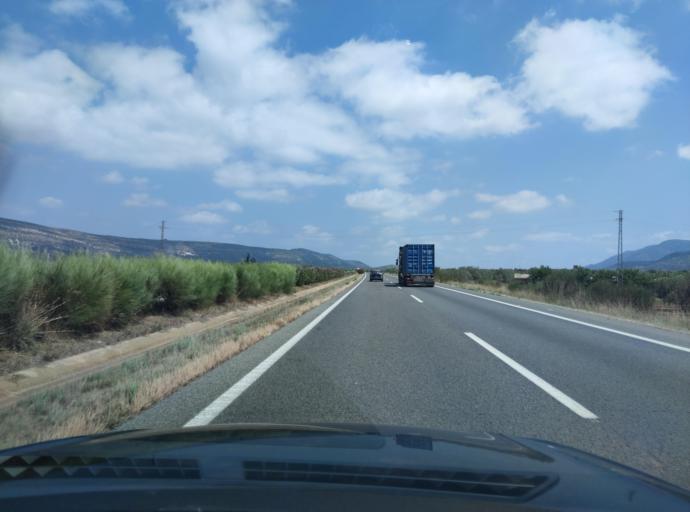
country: ES
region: Catalonia
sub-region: Provincia de Tarragona
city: Ulldecona
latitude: 40.6009
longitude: 0.4722
